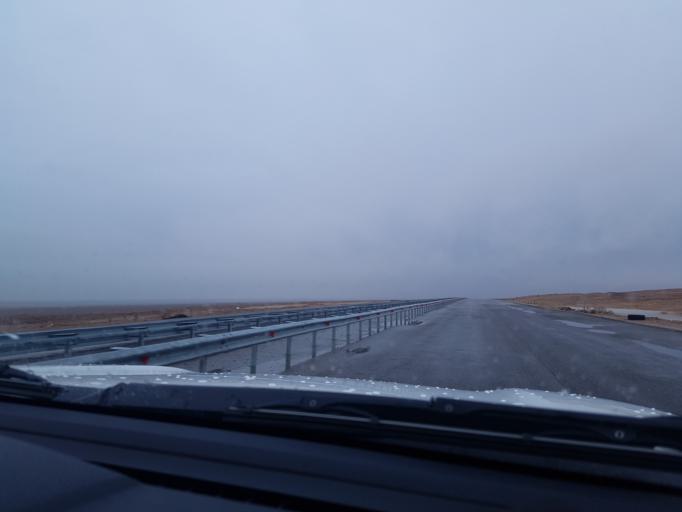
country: TM
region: Balkan
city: Turkmenbasy
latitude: 39.9936
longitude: 53.7390
